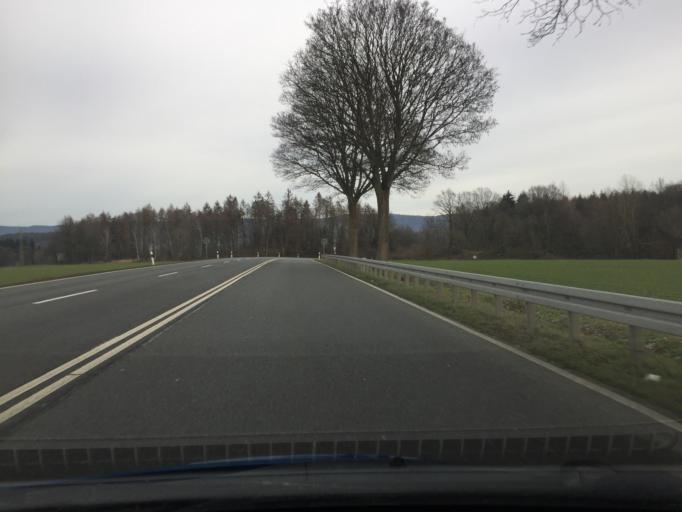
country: DE
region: Lower Saxony
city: Eschershausen
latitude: 51.9166
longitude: 9.6153
